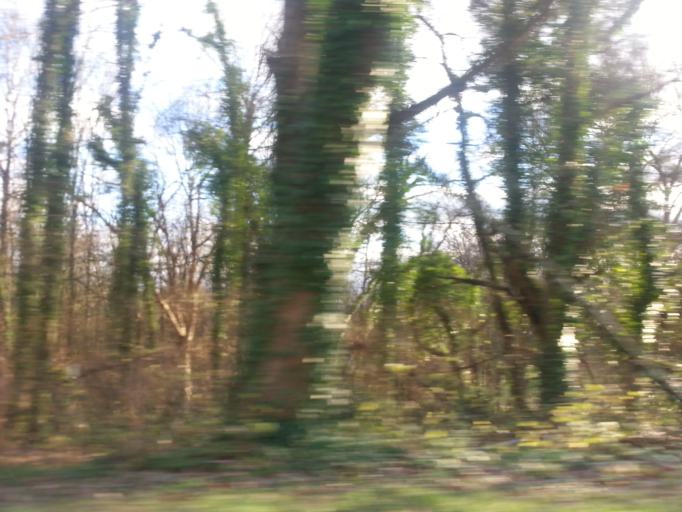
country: US
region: Tennessee
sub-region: Knox County
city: Knoxville
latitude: 36.0013
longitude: -83.8556
